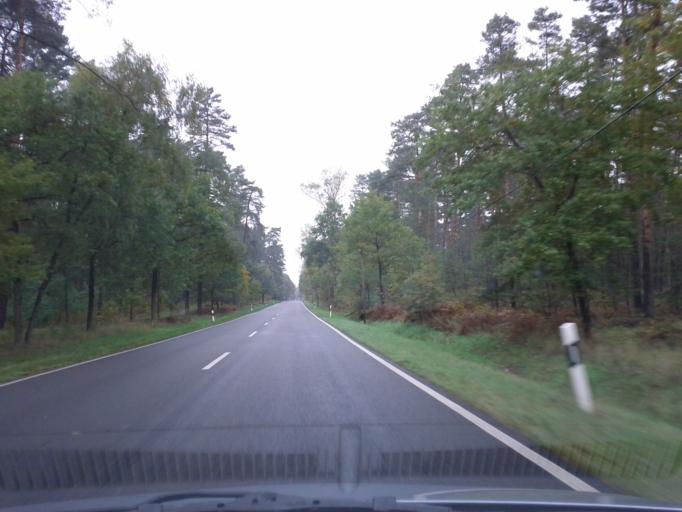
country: DE
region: Brandenburg
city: Grunheide
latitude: 52.4016
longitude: 13.8250
